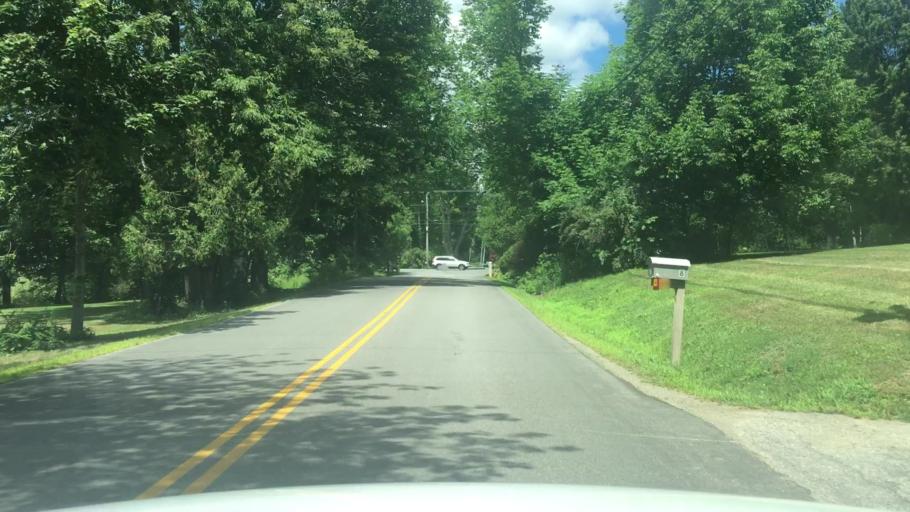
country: US
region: Maine
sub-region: Waldo County
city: Belfast
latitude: 44.4165
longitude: -69.0422
